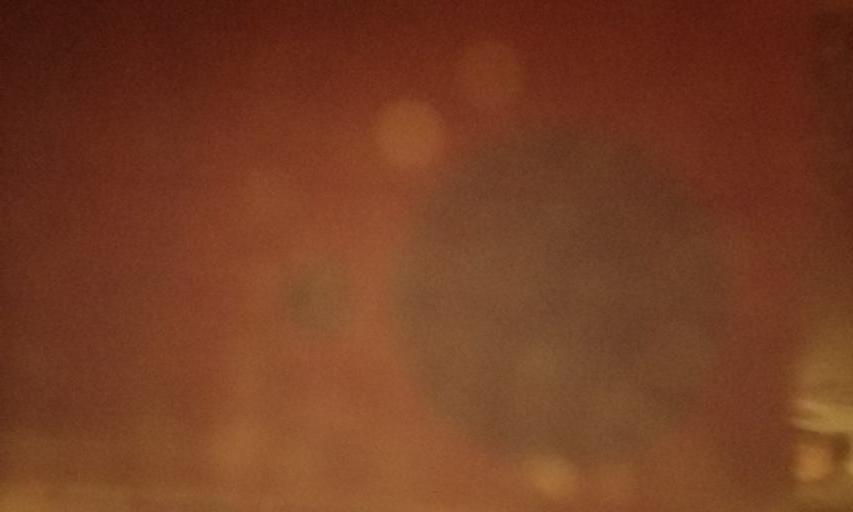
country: JP
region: Okayama
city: Kasaoka
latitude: 34.5267
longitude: 133.4861
